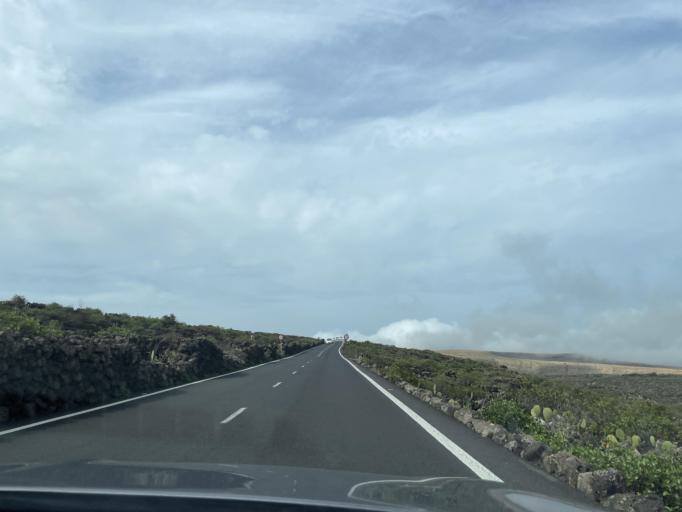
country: ES
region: Canary Islands
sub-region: Provincia de Las Palmas
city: Haria
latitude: 29.1896
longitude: -13.4718
